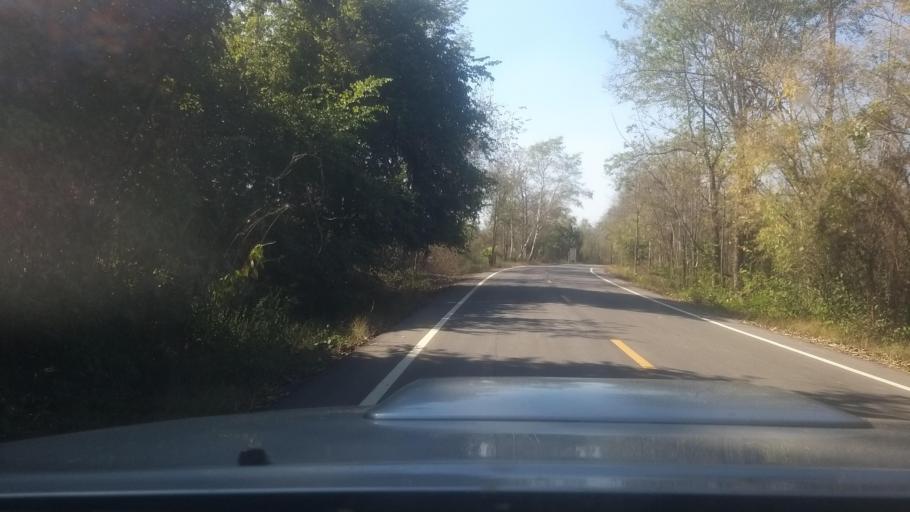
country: TH
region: Phrae
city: Nong Muang Khai
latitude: 18.2950
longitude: 100.0523
